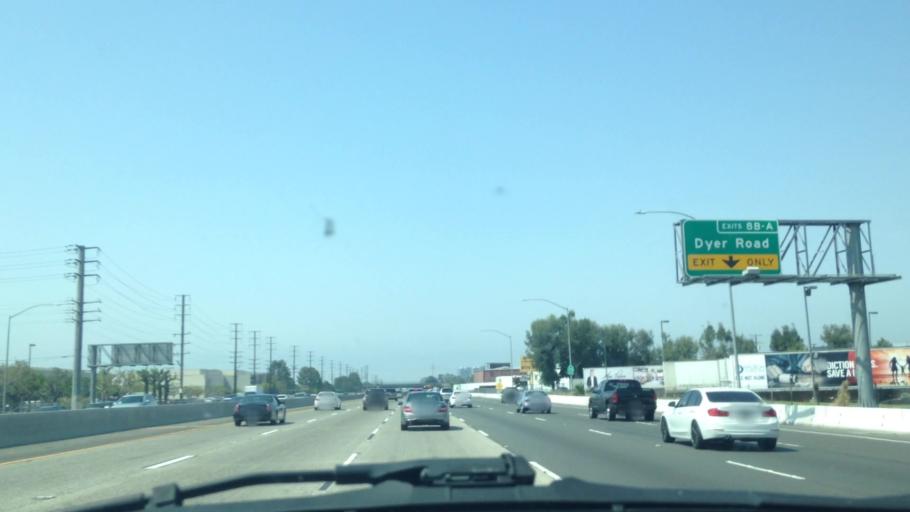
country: US
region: California
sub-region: Orange County
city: Tustin
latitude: 33.7224
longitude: -117.8381
